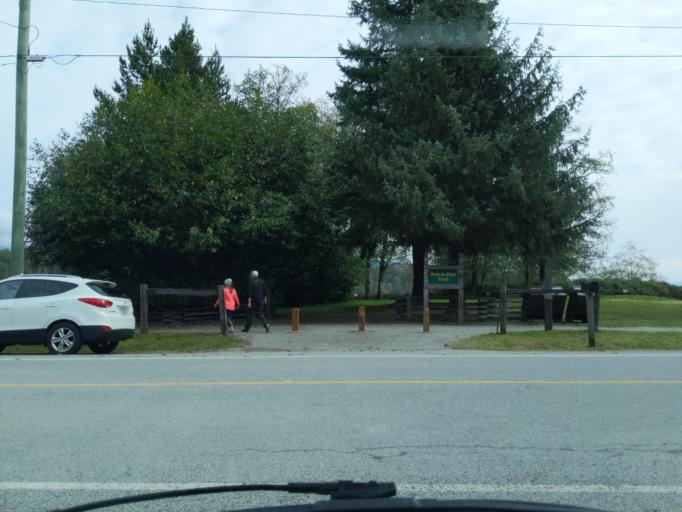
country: CA
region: British Columbia
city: Maple Ridge
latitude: 49.1983
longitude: -122.5943
